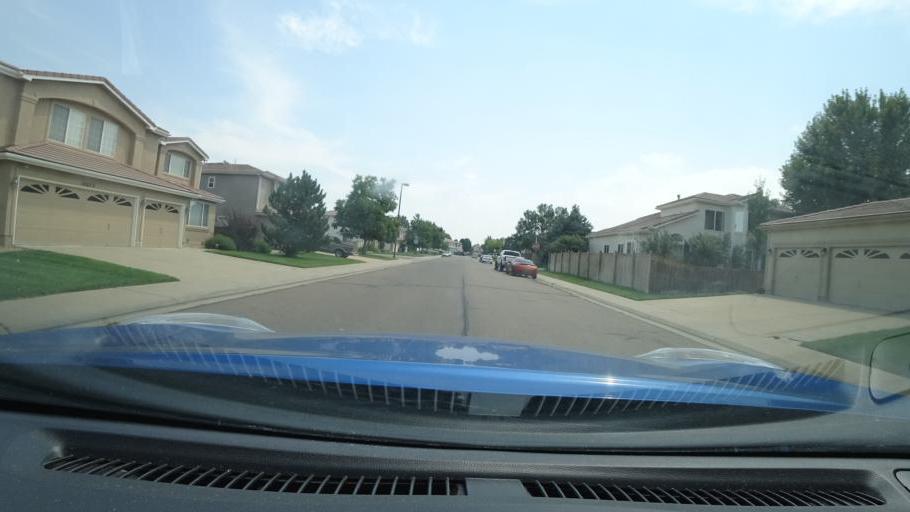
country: US
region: Colorado
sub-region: Adams County
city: Aurora
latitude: 39.7754
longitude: -104.7675
